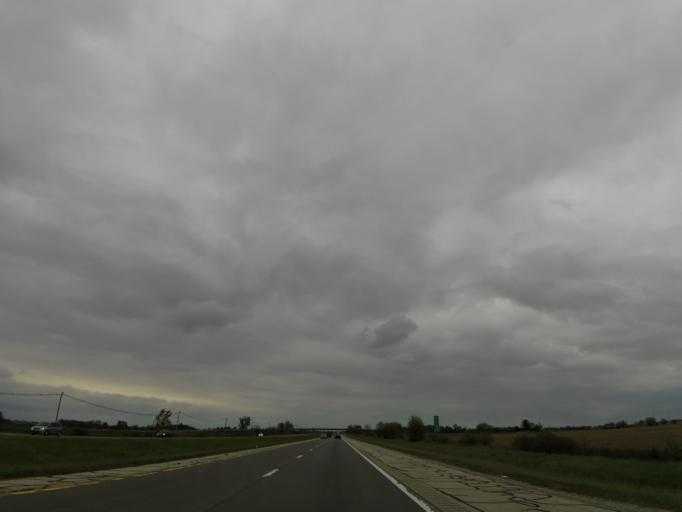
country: US
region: Ohio
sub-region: Fayette County
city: Jeffersonville
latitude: 39.6798
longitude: -83.4877
